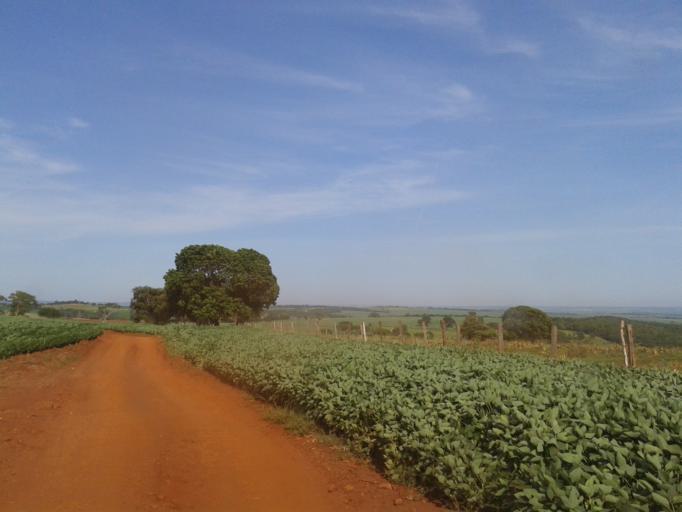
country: BR
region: Minas Gerais
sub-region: Centralina
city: Centralina
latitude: -18.7106
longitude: -49.2042
